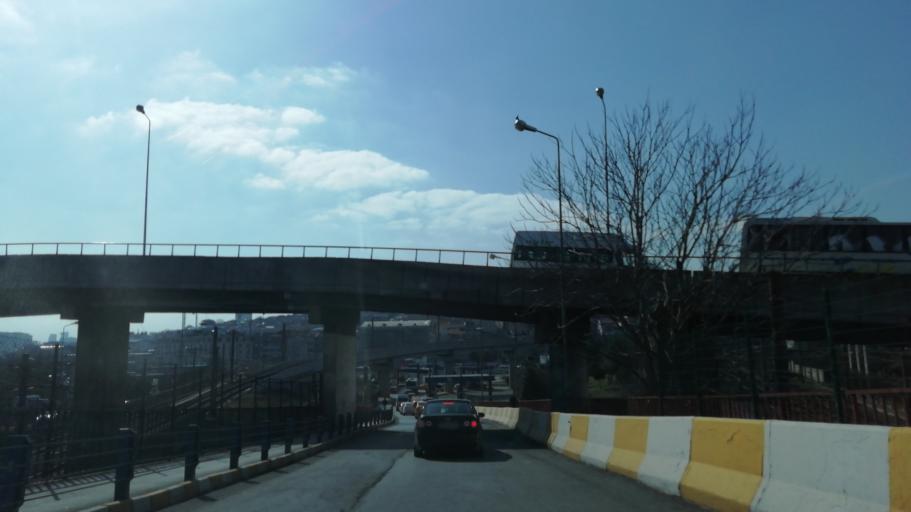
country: TR
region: Istanbul
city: Esenler
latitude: 41.0386
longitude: 28.8941
